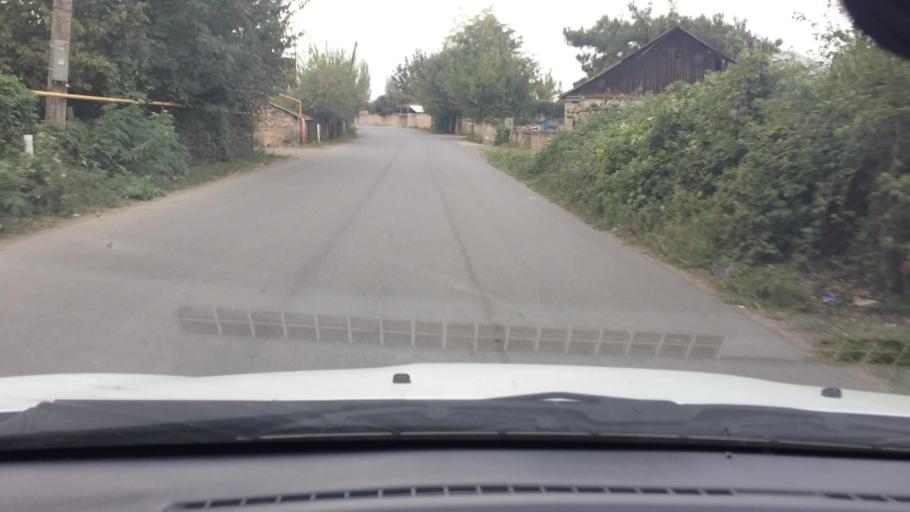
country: AM
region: Tavush
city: Bagratashen
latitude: 41.3405
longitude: 44.8950
